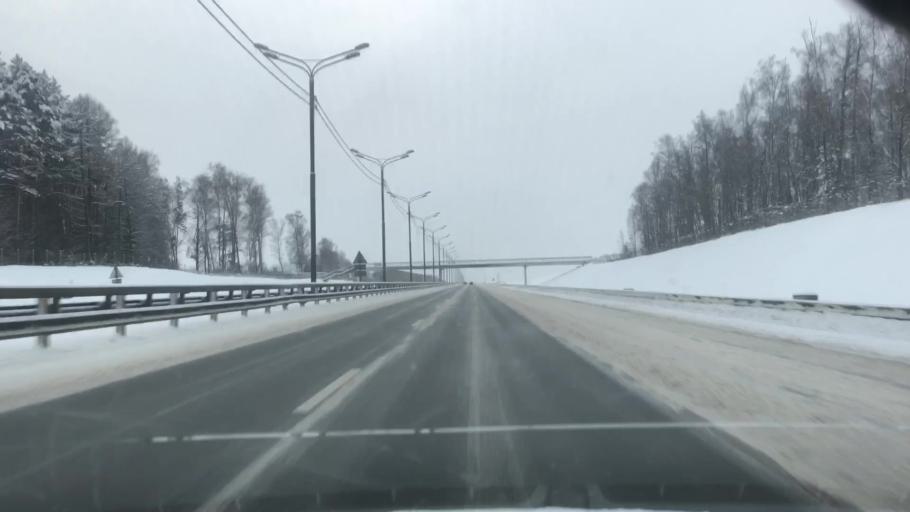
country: RU
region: Moskovskaya
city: Barybino
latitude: 55.2708
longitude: 37.8668
